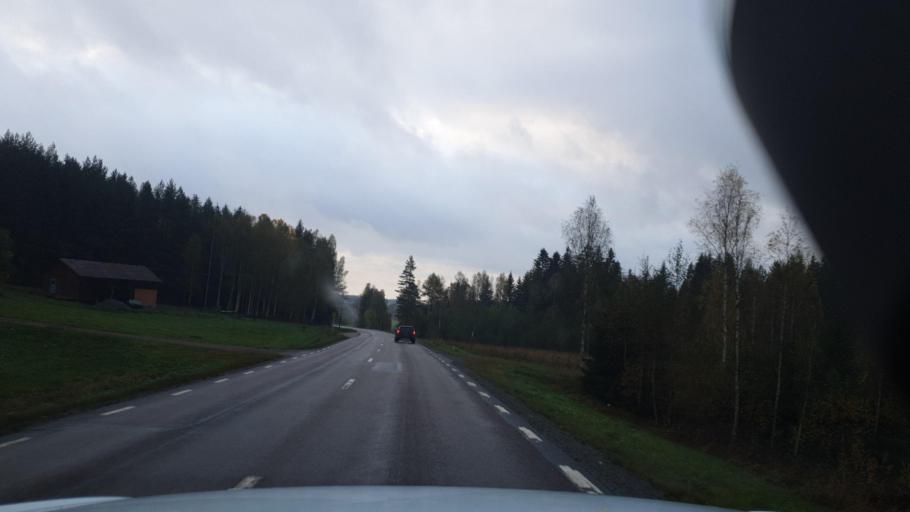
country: SE
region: Vaermland
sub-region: Arvika Kommun
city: Arvika
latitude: 59.6411
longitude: 12.7845
